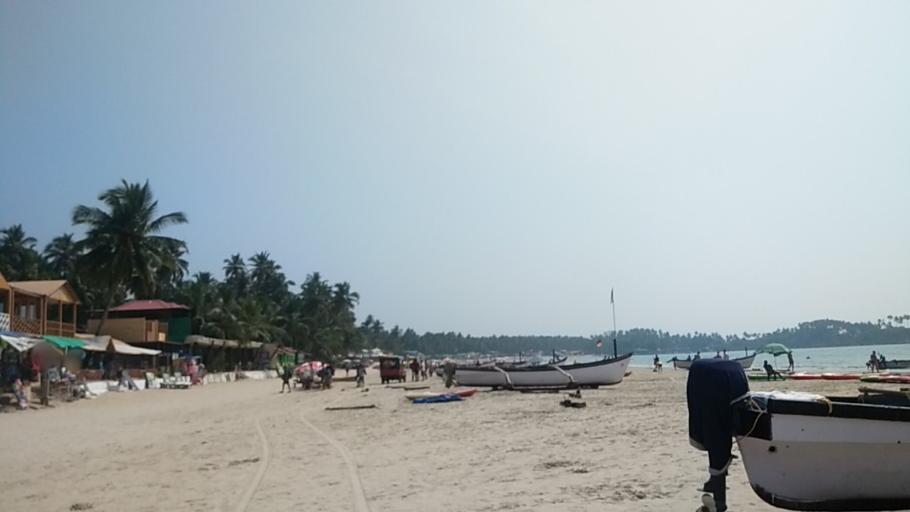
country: IN
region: Goa
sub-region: South Goa
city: Kankon
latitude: 15.0114
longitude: 74.0214
